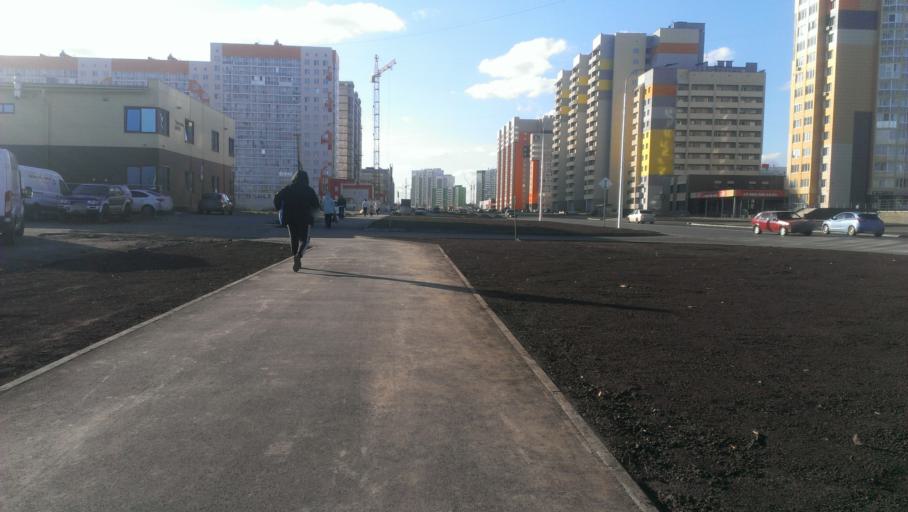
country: RU
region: Altai Krai
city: Novosilikatnyy
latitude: 53.3366
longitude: 83.6619
